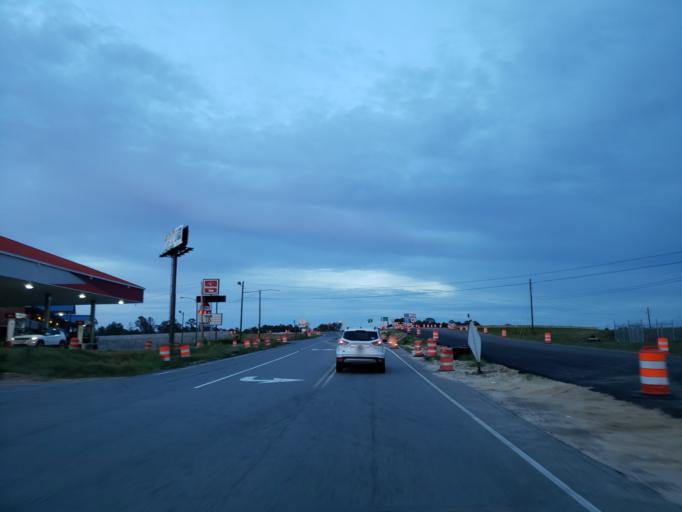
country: US
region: Georgia
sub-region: Lowndes County
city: Hahira
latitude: 30.9930
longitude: -83.3907
